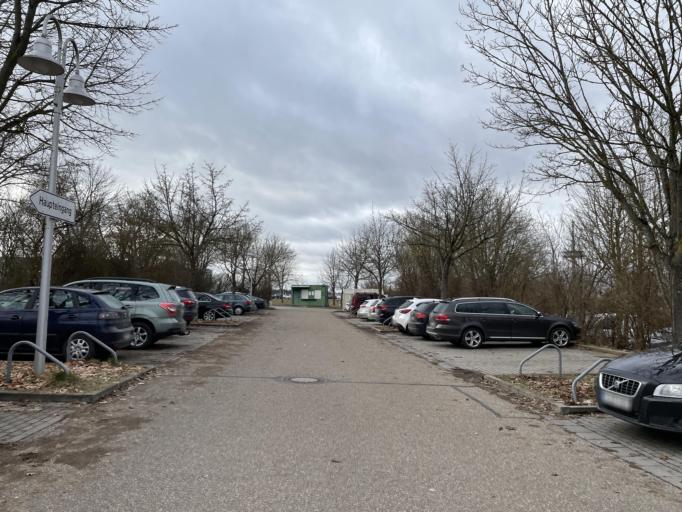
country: DE
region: Bavaria
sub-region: Upper Palatinate
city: Pentling
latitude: 48.9893
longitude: 12.0868
